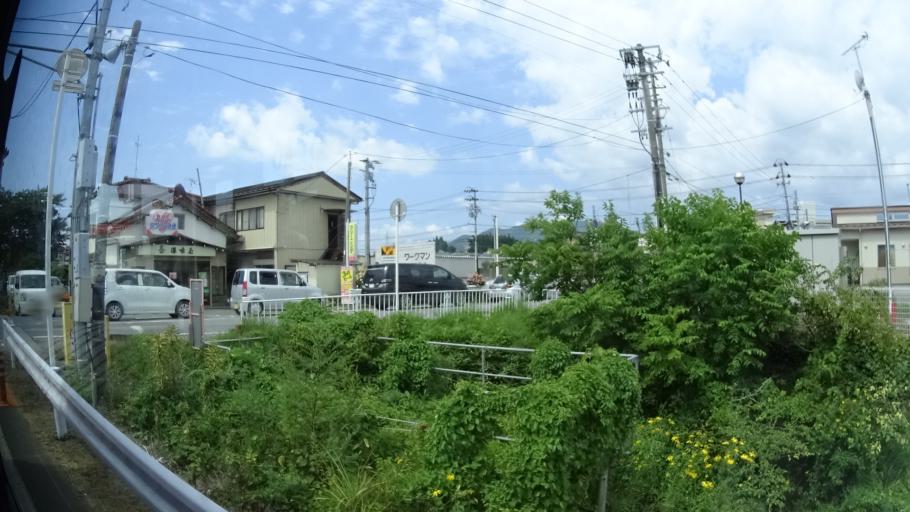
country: JP
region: Iwate
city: Ofunato
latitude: 38.8427
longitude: 141.5814
